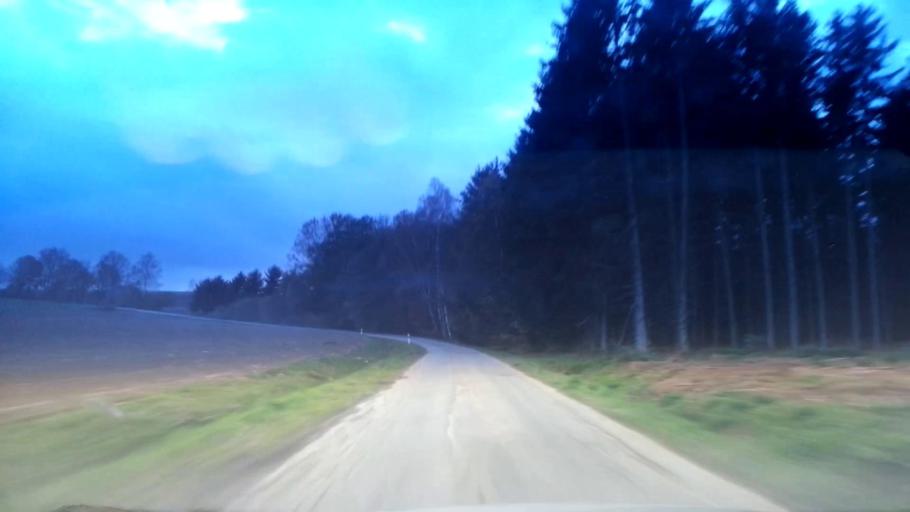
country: DE
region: Bavaria
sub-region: Upper Palatinate
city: Fuchsmuhl
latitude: 49.9255
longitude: 12.1626
